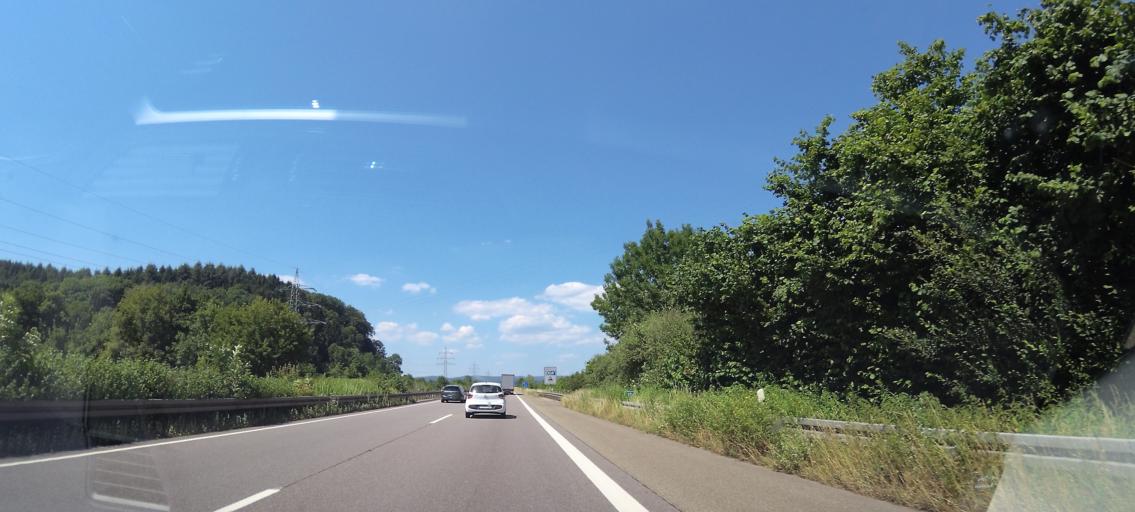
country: DE
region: Saarland
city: Merzig
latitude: 49.4271
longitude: 6.6306
